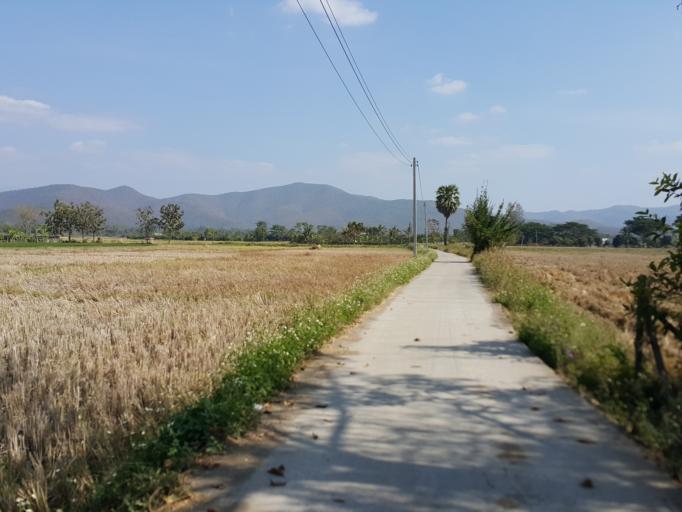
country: TH
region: Chiang Mai
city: San Kamphaeng
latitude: 18.8076
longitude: 99.1614
